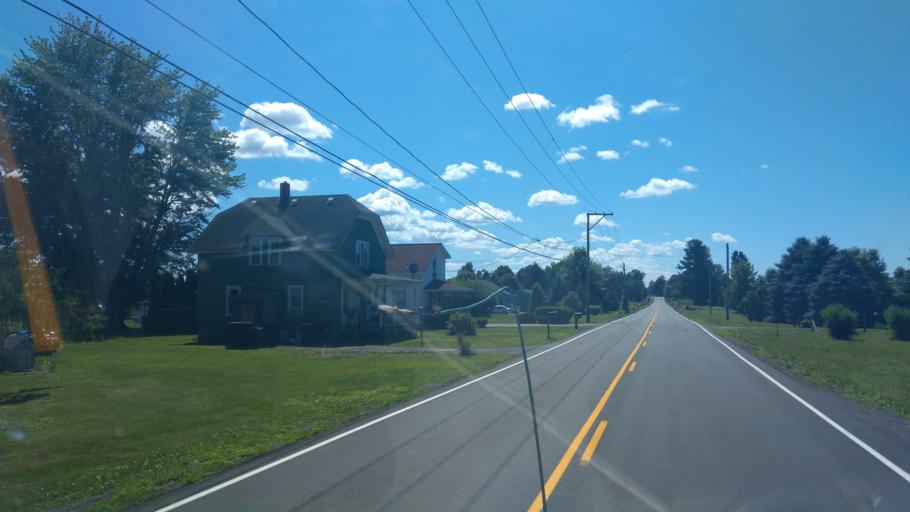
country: US
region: New York
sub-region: Wayne County
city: Sodus
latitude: 43.2043
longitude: -77.0325
